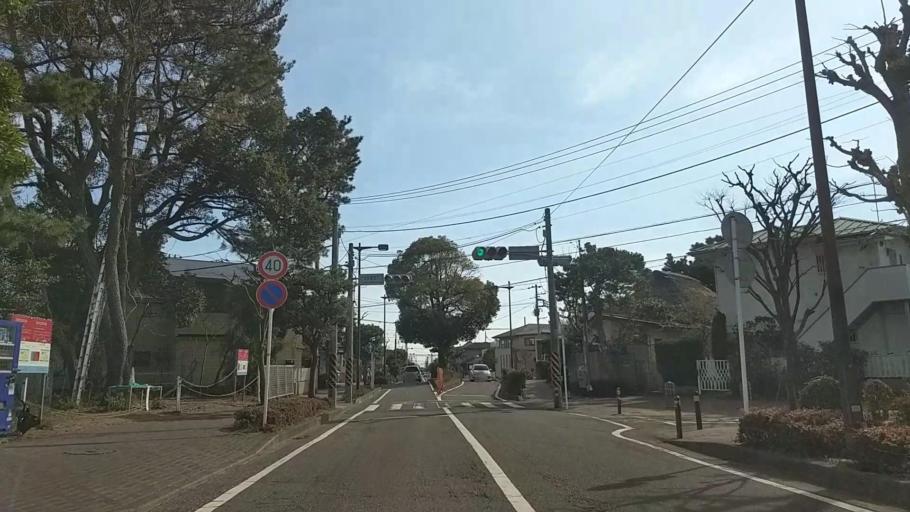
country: JP
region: Kanagawa
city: Fujisawa
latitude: 35.3342
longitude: 139.4472
